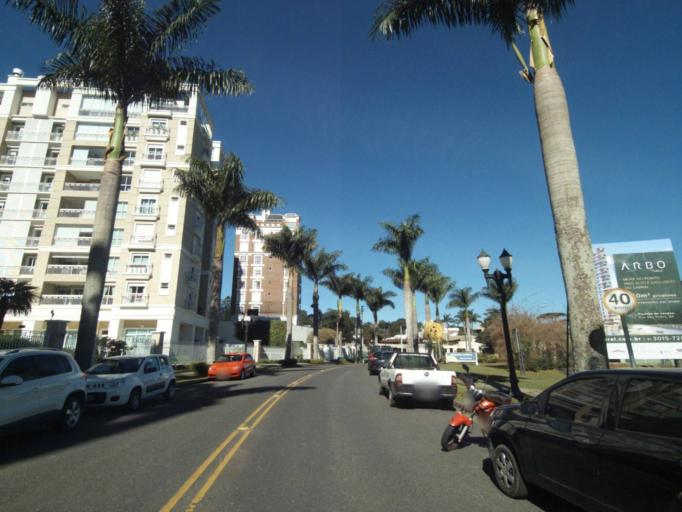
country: BR
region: Parana
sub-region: Curitiba
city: Curitiba
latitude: -25.4119
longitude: -49.2430
